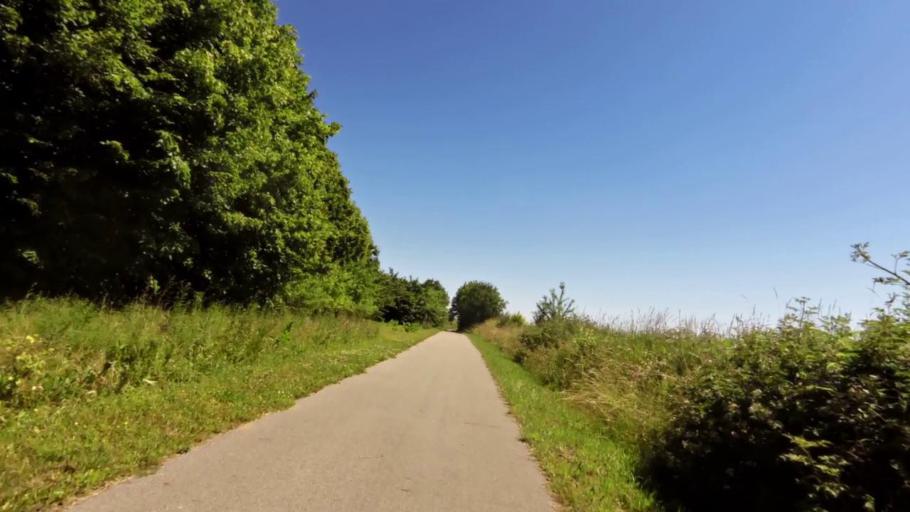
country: PL
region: West Pomeranian Voivodeship
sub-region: Powiat kolobrzeski
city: Goscino
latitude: 54.0397
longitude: 15.6617
